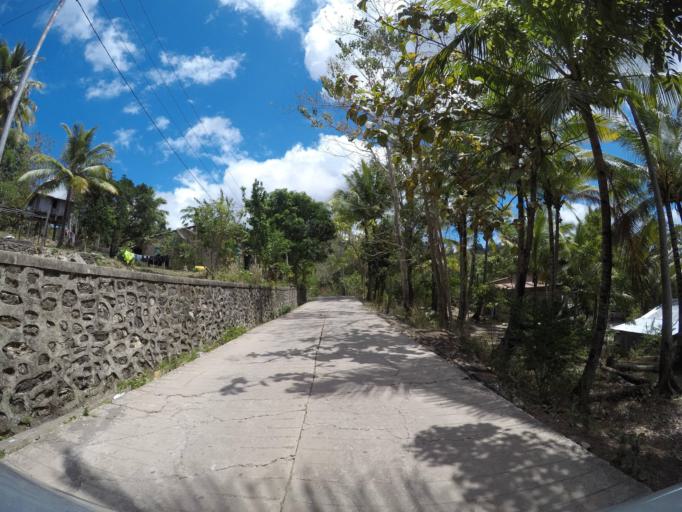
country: TL
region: Lautem
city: Lospalos
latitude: -8.5434
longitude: 126.8321
